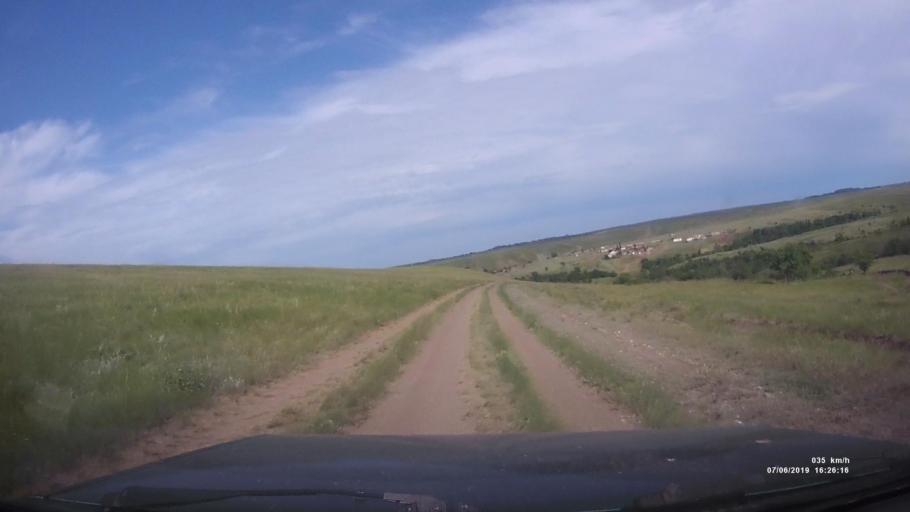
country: RU
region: Rostov
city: Kamensk-Shakhtinskiy
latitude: 48.2527
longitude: 40.3101
